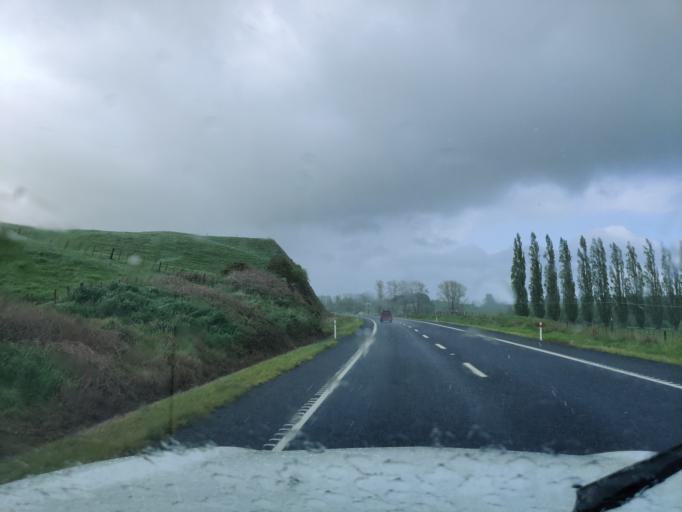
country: NZ
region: Waikato
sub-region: Matamata-Piako District
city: Matamata
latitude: -37.9680
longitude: 175.6900
